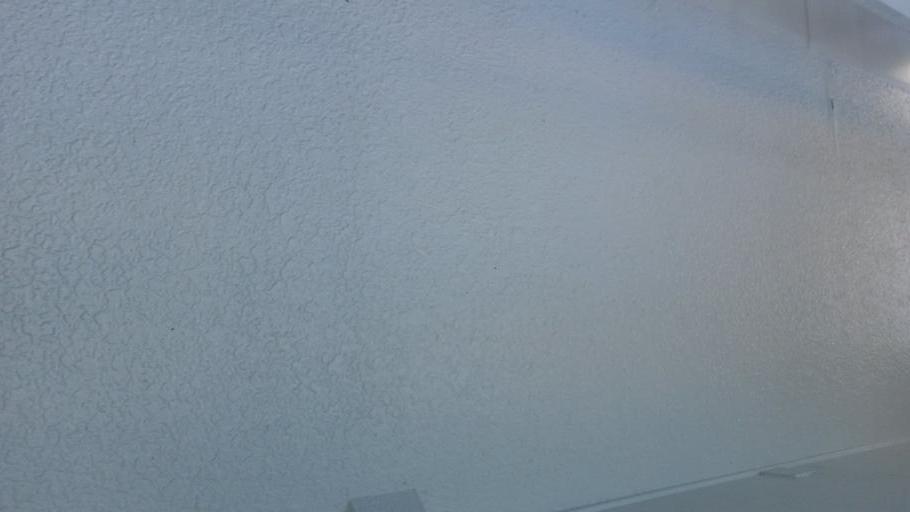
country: HR
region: Dubrovacko-Neretvanska
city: Smokvica
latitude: 42.7457
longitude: 16.8244
